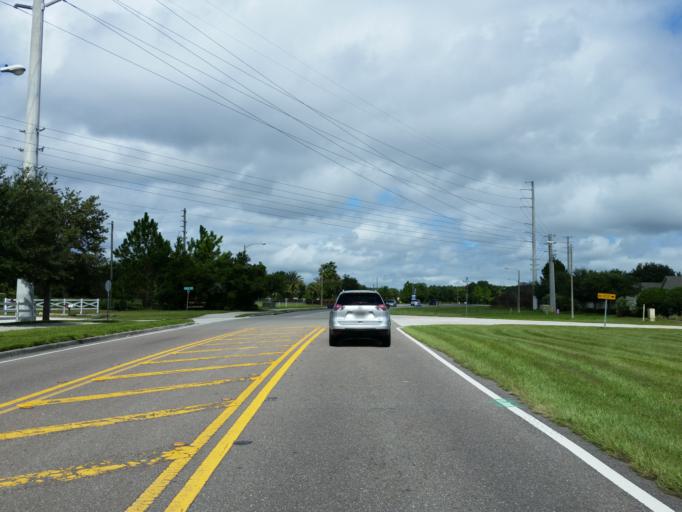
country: US
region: Florida
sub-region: Pasco County
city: Wesley Chapel
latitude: 28.2179
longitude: -82.3033
